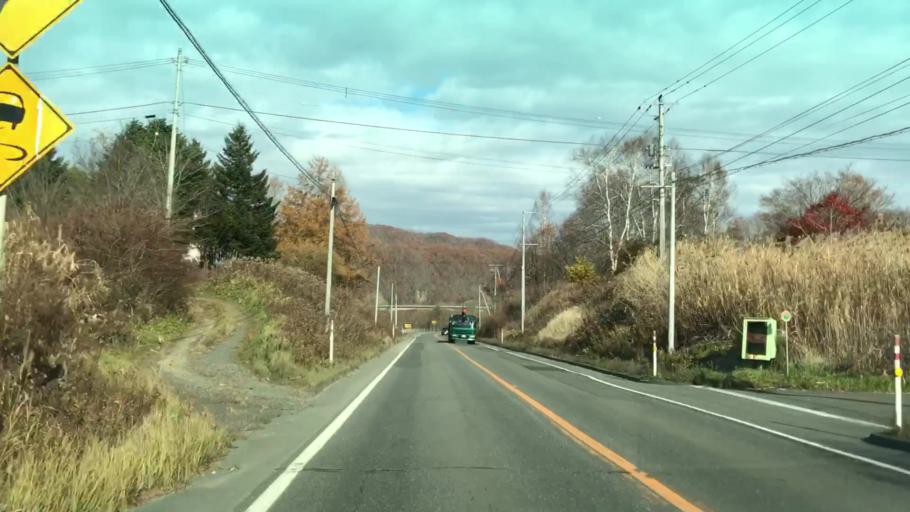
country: JP
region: Hokkaido
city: Shizunai-furukawacho
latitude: 42.6668
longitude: 142.1809
